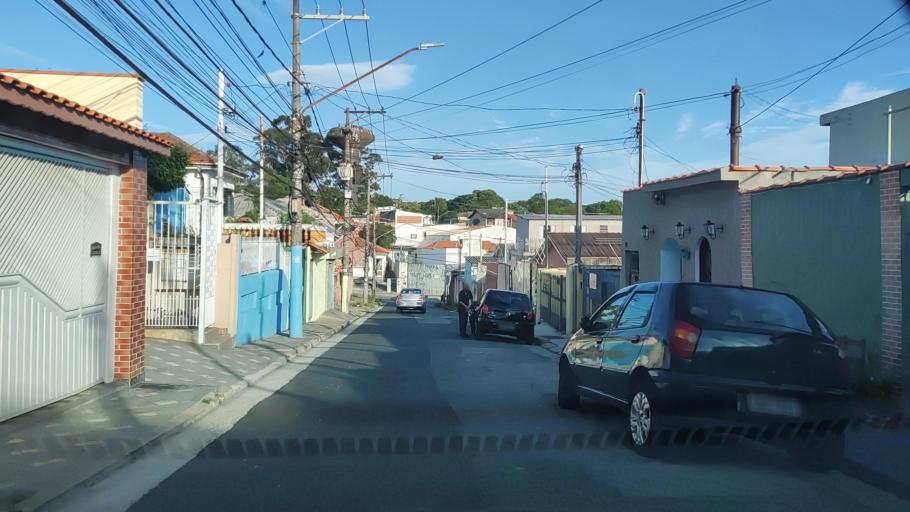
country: BR
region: Sao Paulo
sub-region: Osasco
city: Osasco
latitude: -23.5117
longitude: -46.7548
